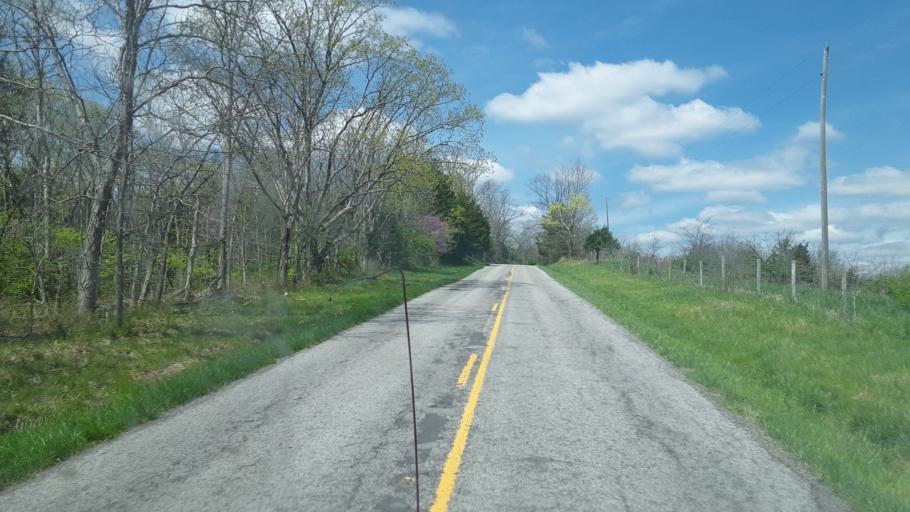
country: US
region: Kentucky
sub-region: Grant County
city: Dry Ridge
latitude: 38.6468
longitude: -84.7340
